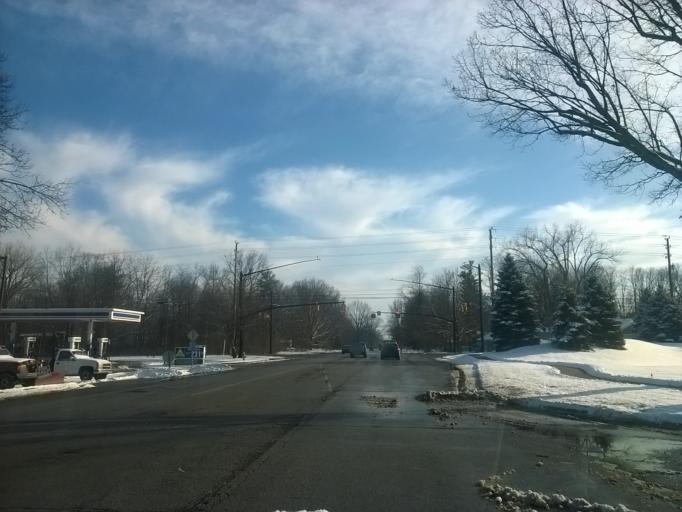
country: US
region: Indiana
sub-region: Marion County
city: Meridian Hills
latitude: 39.9281
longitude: -86.1459
